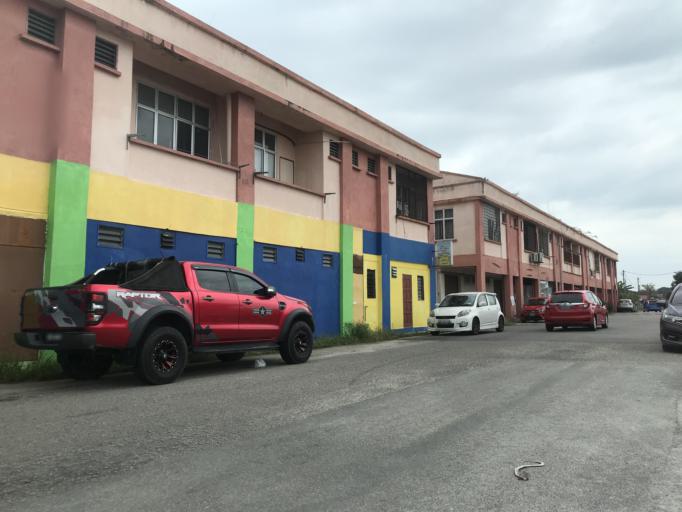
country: MY
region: Kelantan
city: Kota Bharu
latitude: 6.1202
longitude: 102.2182
